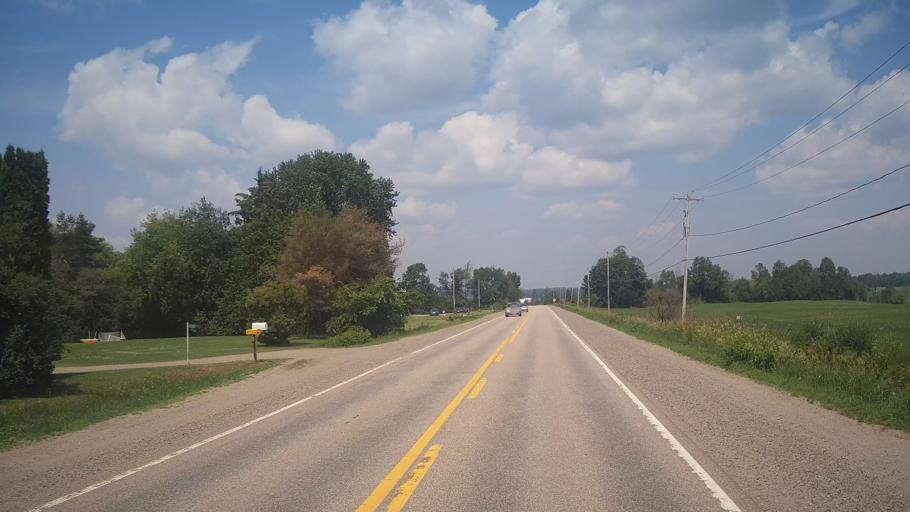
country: CA
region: Quebec
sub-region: Outaouais
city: Shawville
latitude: 45.5789
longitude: -76.4496
